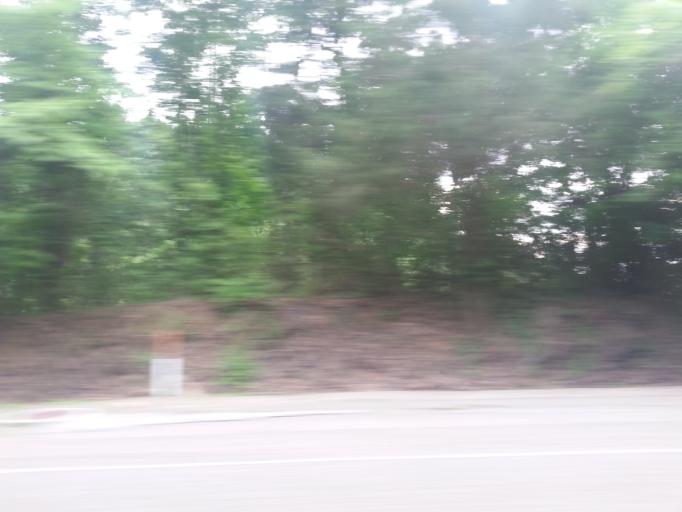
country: US
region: Tennessee
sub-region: Knox County
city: Knoxville
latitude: 35.9974
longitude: -83.9531
